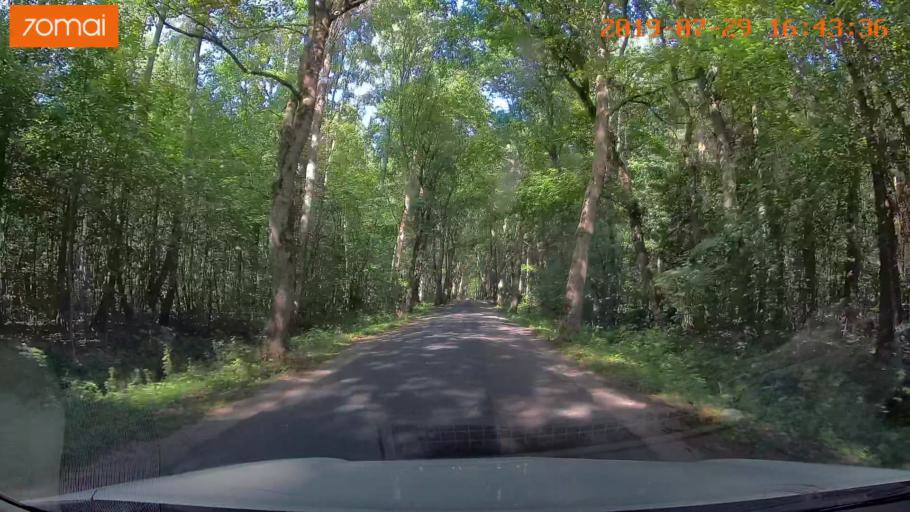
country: RU
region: Kaliningrad
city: Primorsk
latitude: 54.7499
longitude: 20.0860
